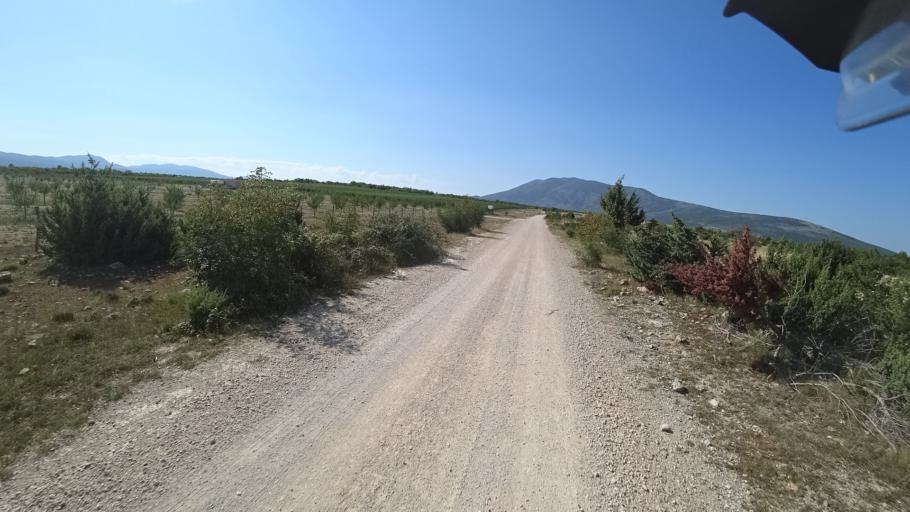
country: HR
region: Sibensko-Kniniska
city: Knin
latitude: 43.9927
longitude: 16.1930
